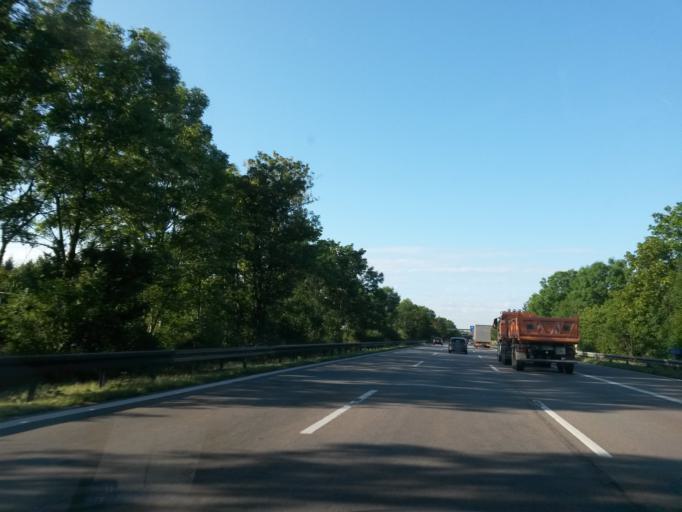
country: DE
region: Bavaria
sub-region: Upper Bavaria
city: Vaterstetten
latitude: 48.1230
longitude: 11.7585
